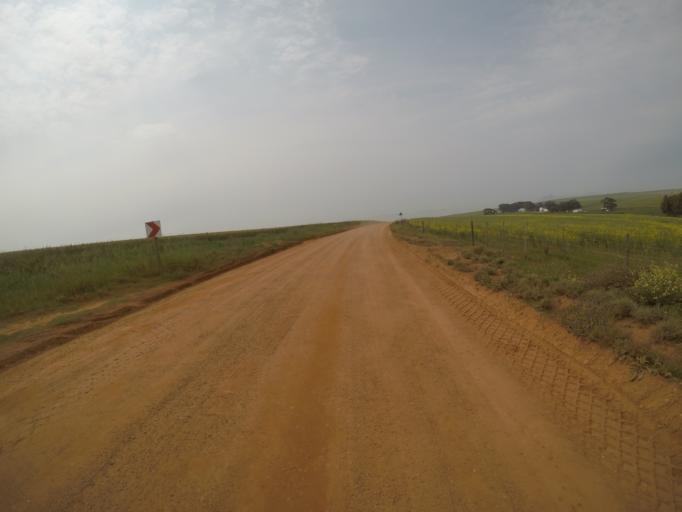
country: ZA
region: Western Cape
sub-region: City of Cape Town
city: Kraaifontein
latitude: -33.7235
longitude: 18.6568
